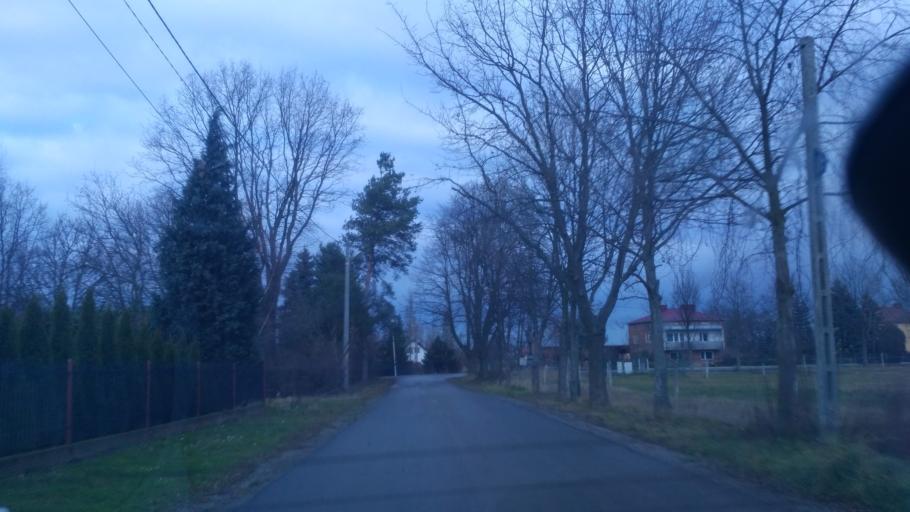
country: PL
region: Subcarpathian Voivodeship
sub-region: Powiat lancucki
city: Czarna
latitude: 50.0982
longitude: 22.1803
